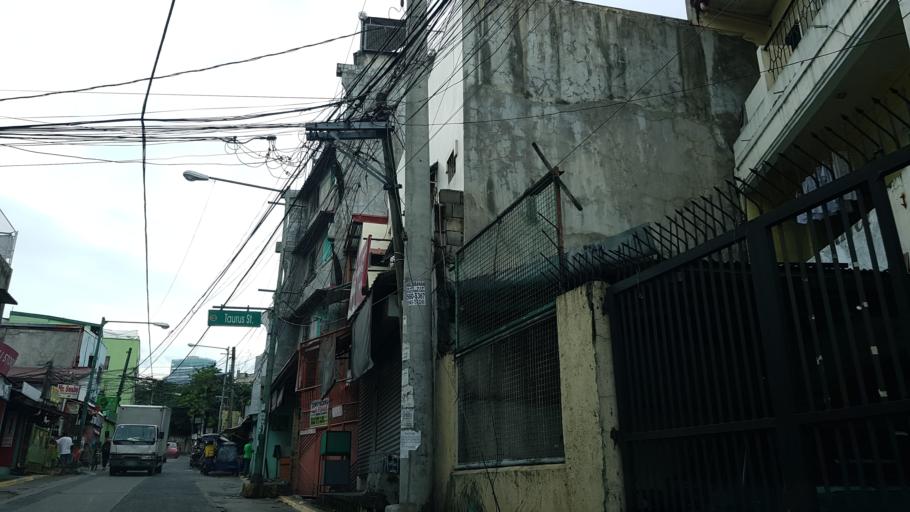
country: PH
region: Calabarzon
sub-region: Province of Rizal
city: Pateros
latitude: 14.5442
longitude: 121.0579
